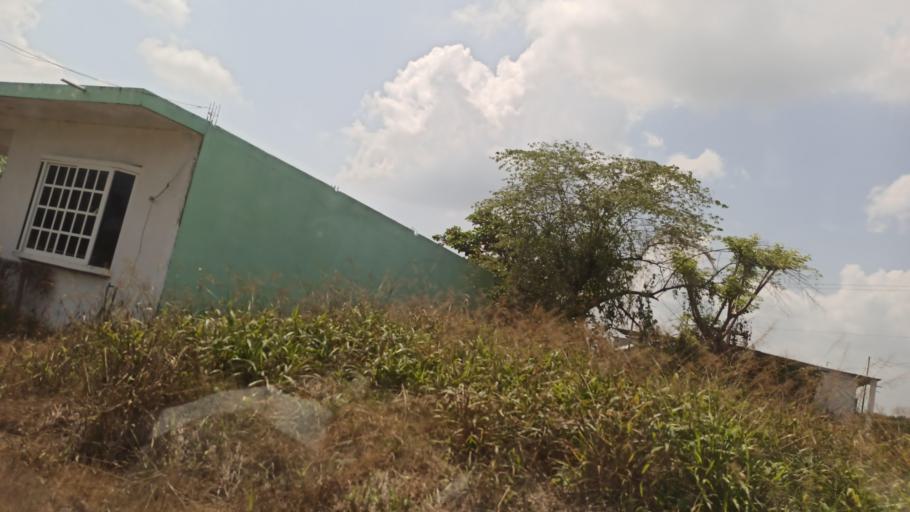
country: MX
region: Puebla
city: San Jose Acateno
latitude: 20.1762
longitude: -97.1134
